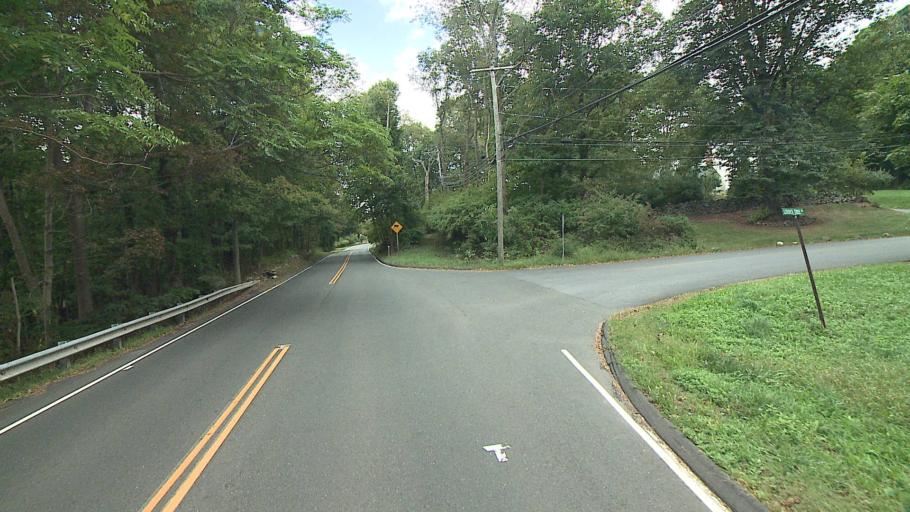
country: US
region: Connecticut
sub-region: Fairfield County
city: Wilton
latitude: 41.2136
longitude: -73.4696
